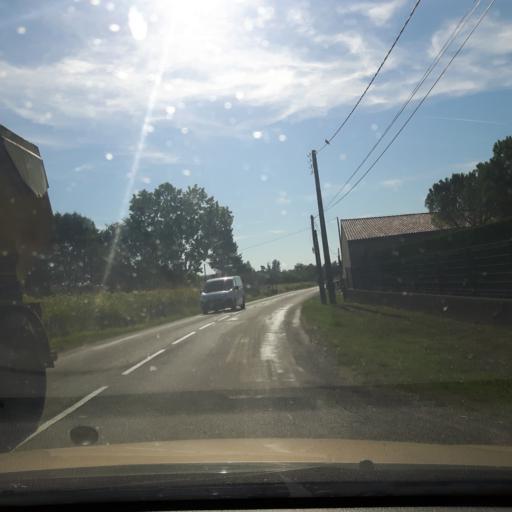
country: FR
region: Midi-Pyrenees
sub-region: Departement de la Haute-Garonne
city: Bouloc
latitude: 43.7670
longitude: 1.4006
